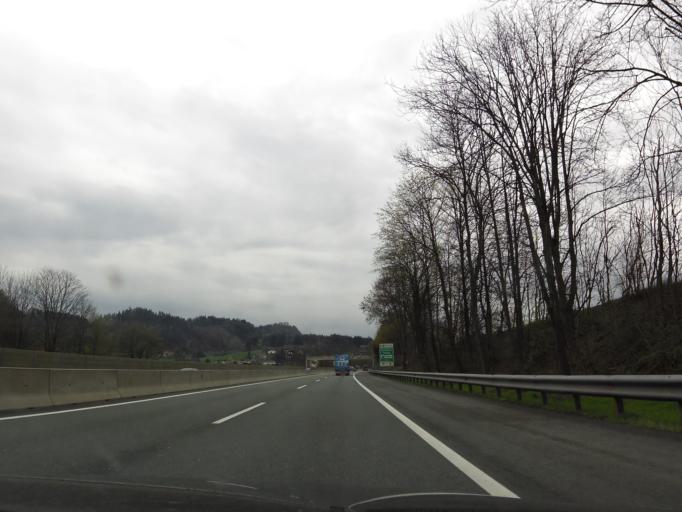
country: AT
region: Tyrol
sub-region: Politischer Bezirk Kufstein
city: Kufstein
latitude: 47.5820
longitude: 12.1514
